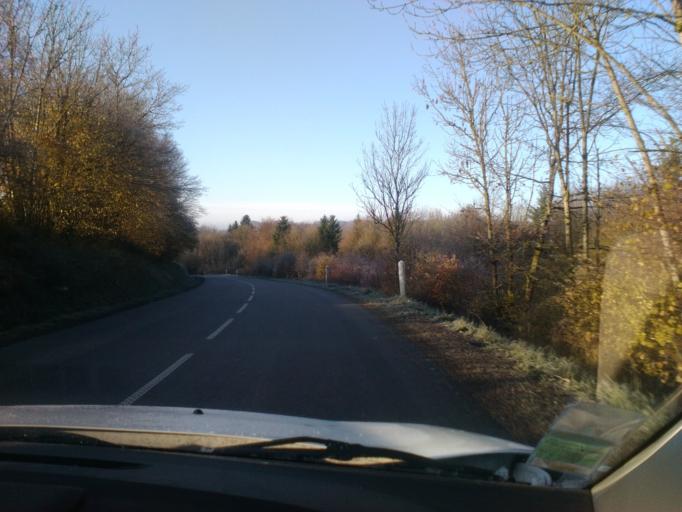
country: FR
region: Lorraine
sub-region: Departement des Vosges
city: Darnieulles
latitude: 48.1840
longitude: 6.2145
